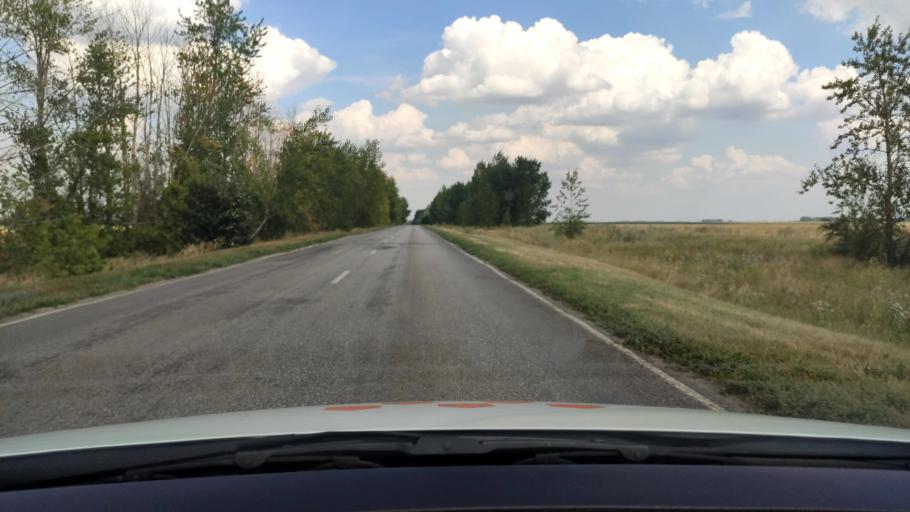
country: RU
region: Voronezj
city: Pereleshinskiy
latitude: 51.7206
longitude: 40.3555
